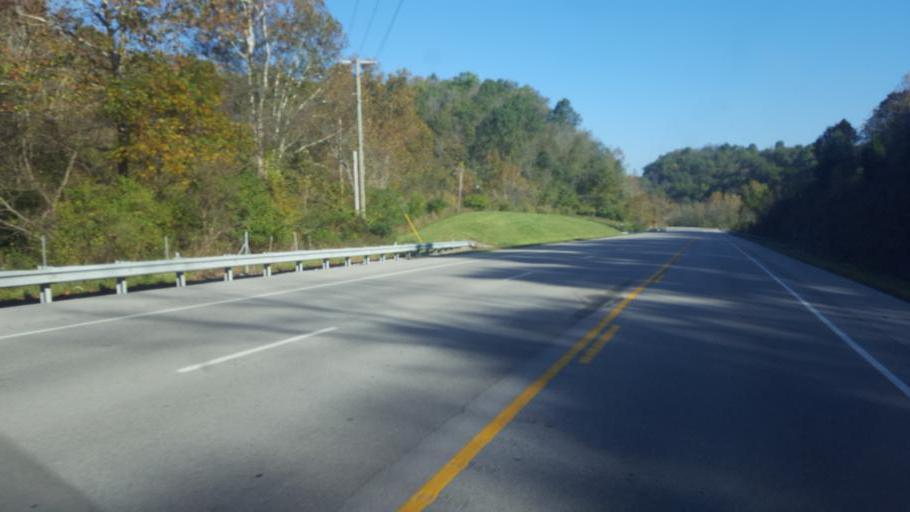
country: US
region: Kentucky
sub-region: Mason County
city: Maysville
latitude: 38.6151
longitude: -83.7546
